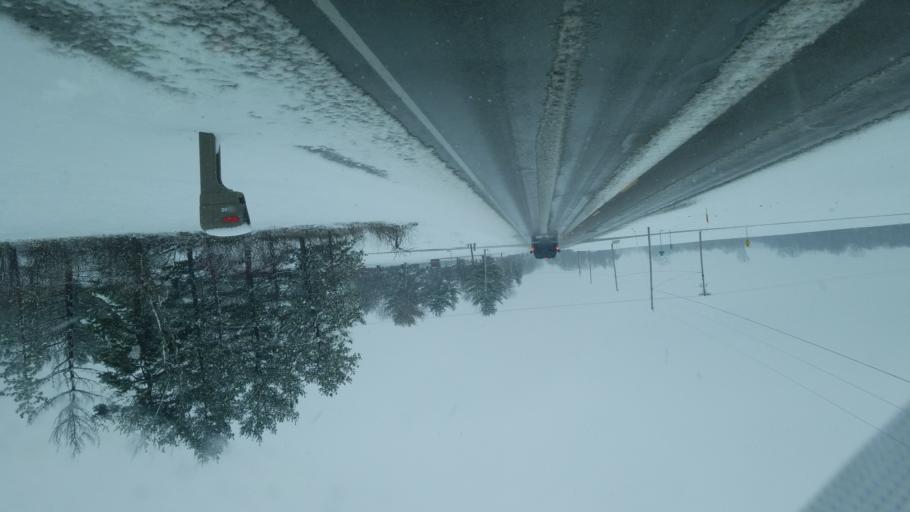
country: US
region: Indiana
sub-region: Delaware County
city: Muncie
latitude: 40.0994
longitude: -85.3159
